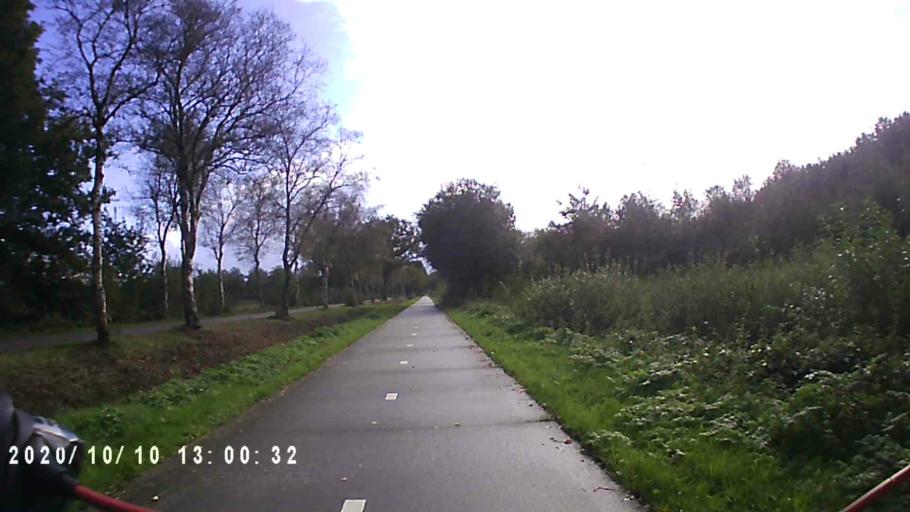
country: NL
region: Drenthe
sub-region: Gemeente Westerveld
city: Dwingeloo
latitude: 52.8973
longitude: 6.3025
